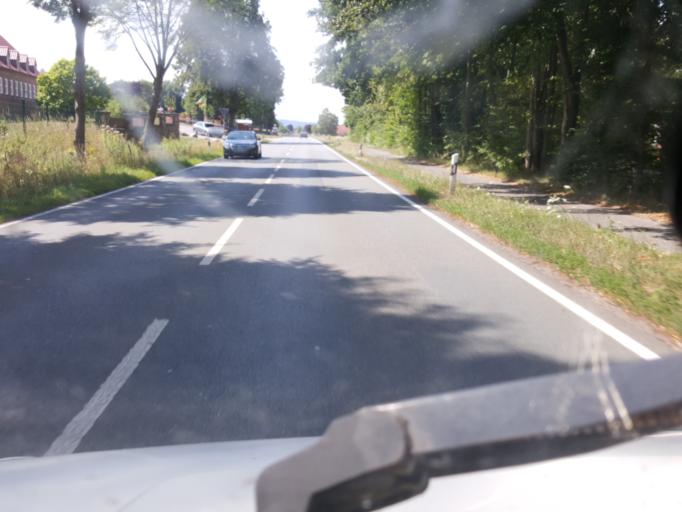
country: DE
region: North Rhine-Westphalia
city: Bad Oeynhausen
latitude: 52.2637
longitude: 8.8470
